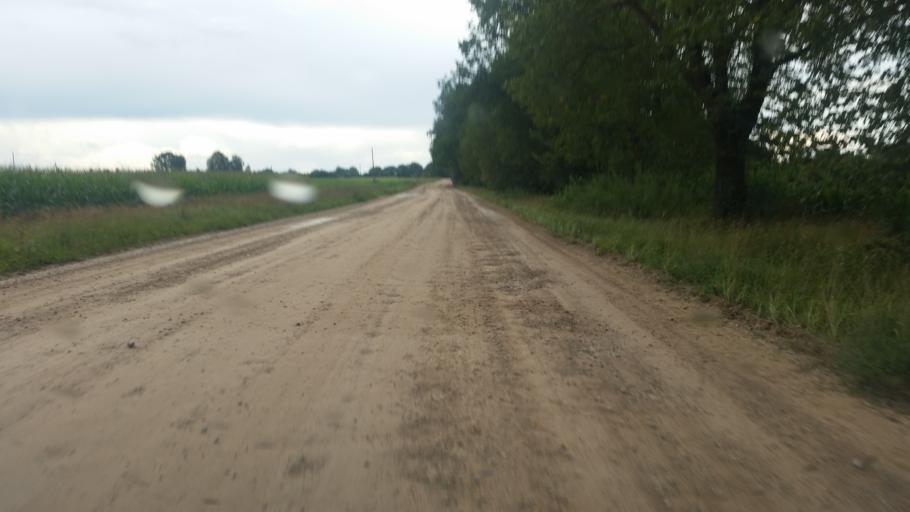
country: LV
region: Vecumnieki
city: Vecumnieki
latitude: 56.4562
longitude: 24.6057
